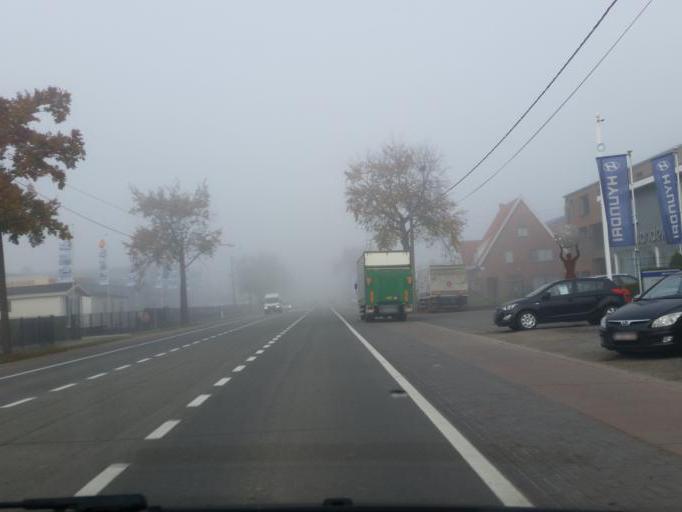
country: BE
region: Flanders
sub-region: Provincie Oost-Vlaanderen
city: Wetteren
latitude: 50.9822
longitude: 3.8494
